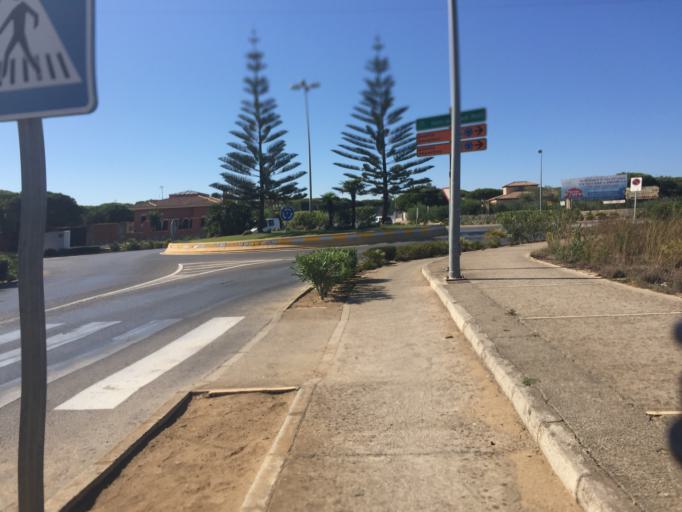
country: ES
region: Andalusia
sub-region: Provincia de Cadiz
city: Chiclana de la Frontera
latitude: 36.3841
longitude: -6.1896
